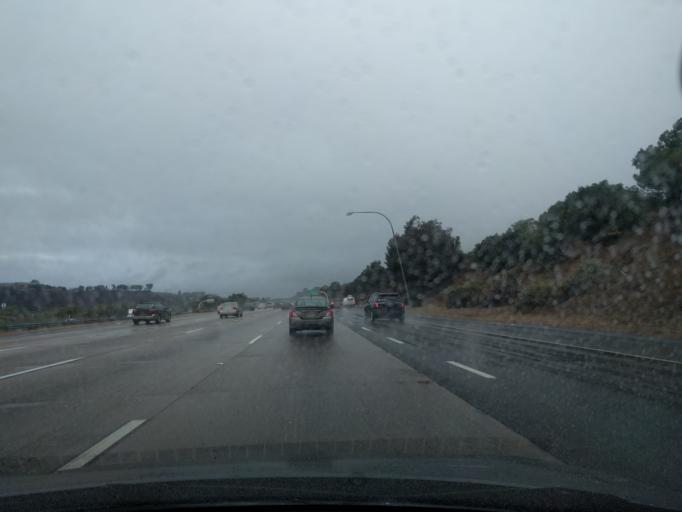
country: US
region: California
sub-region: San Diego County
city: La Mesa
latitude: 32.8106
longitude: -117.1138
